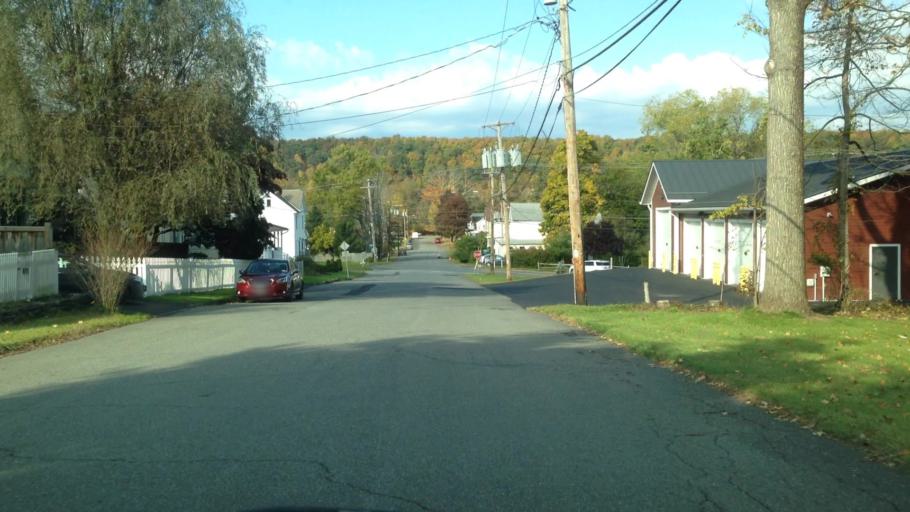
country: US
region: New York
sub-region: Ulster County
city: Tillson
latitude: 41.8378
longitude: -74.0390
